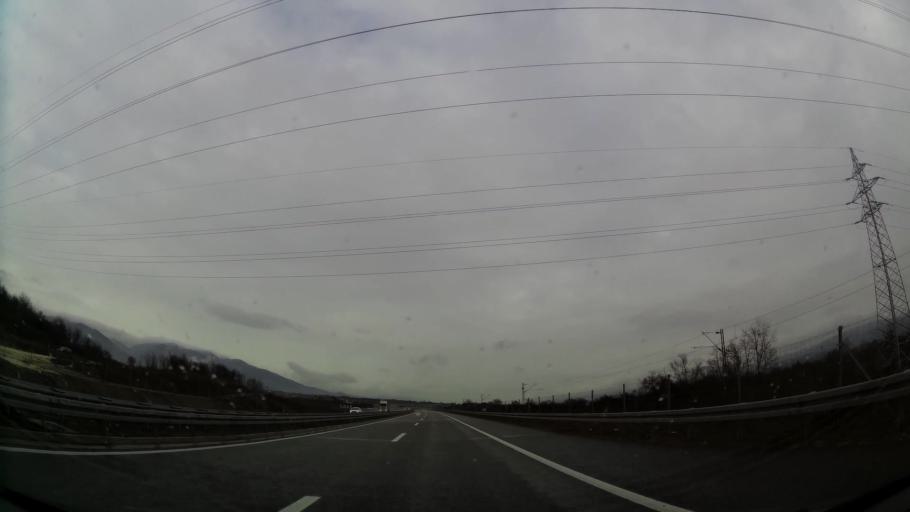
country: RS
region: Central Serbia
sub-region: Pcinjski Okrug
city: Vranje
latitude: 42.5115
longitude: 21.8870
